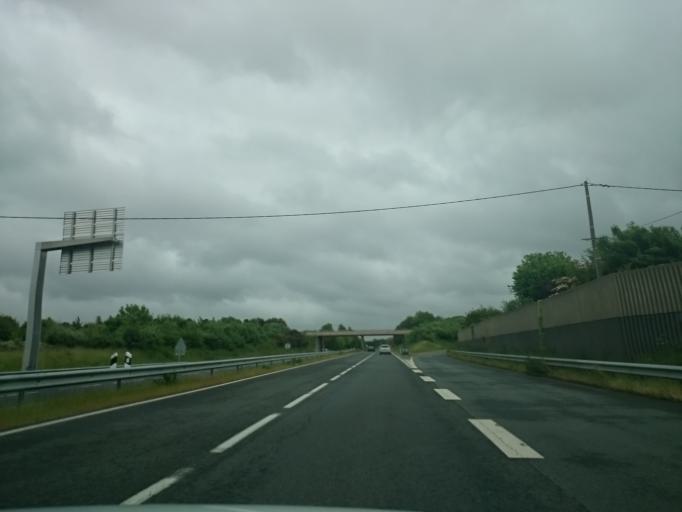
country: FR
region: Brittany
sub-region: Departement des Cotes-d'Armor
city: Cavan
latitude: 48.6598
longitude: -3.3387
